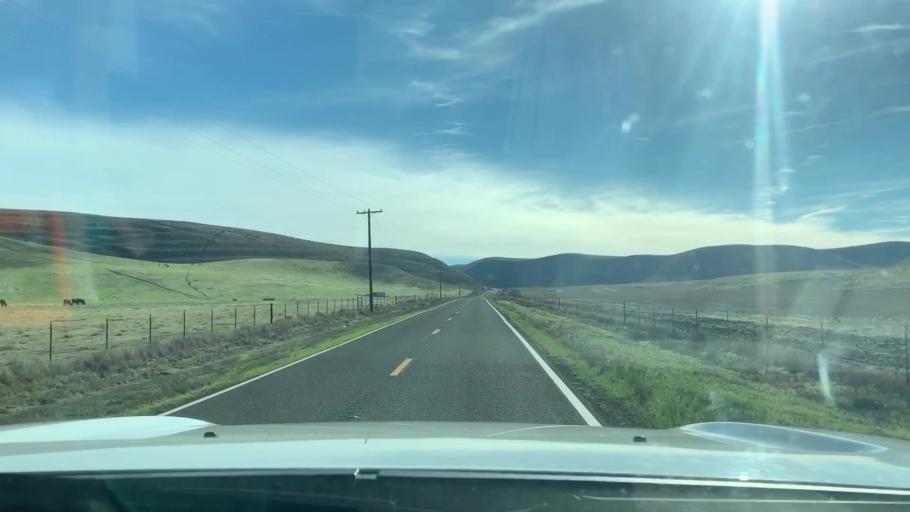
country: US
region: California
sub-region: Monterey County
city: King City
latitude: 36.1565
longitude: -120.9784
